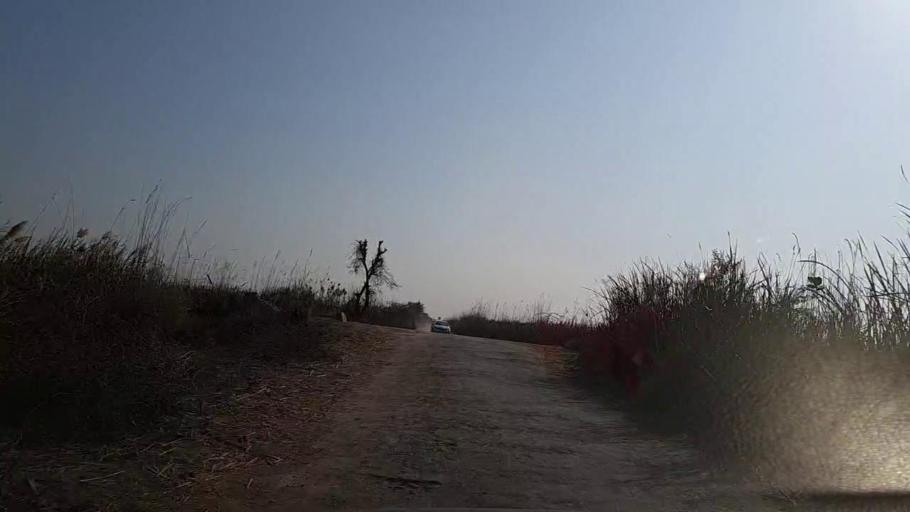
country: PK
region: Sindh
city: Tando Mittha Khan
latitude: 25.8921
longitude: 69.0769
